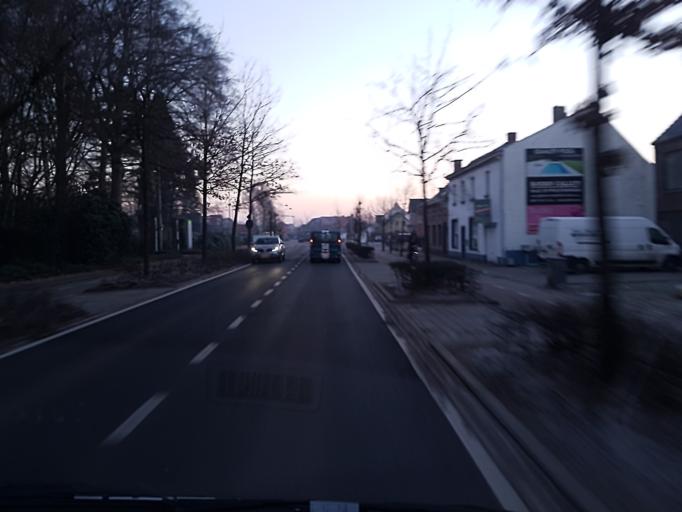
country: BE
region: Flanders
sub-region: Provincie Antwerpen
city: Schilde
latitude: 51.2586
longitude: 4.6252
